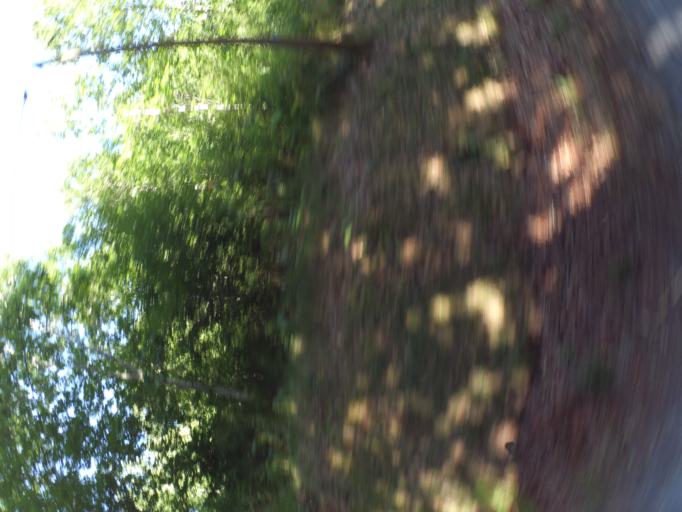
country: FR
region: Limousin
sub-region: Departement de la Correze
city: Bugeat
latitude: 45.6945
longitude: 1.9105
